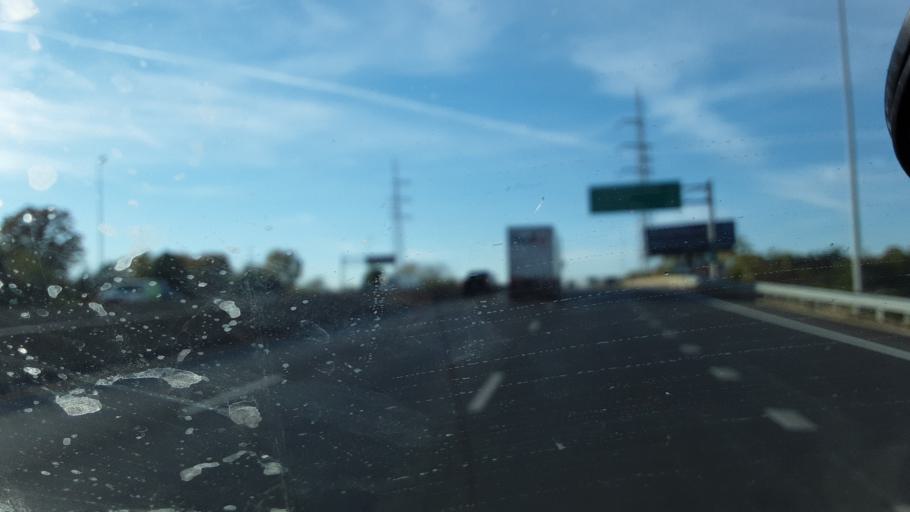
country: US
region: Missouri
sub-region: Saint Louis County
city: Pine Lawn
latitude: 38.6839
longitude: -90.2402
